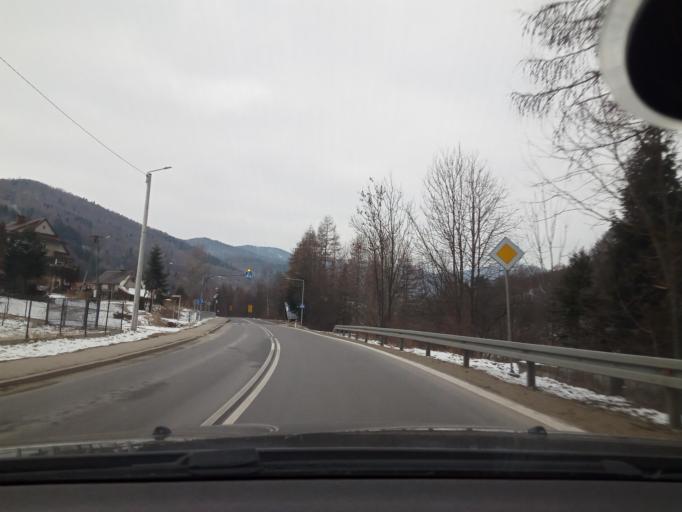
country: PL
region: Lesser Poland Voivodeship
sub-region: Powiat nowotarski
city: Kroscienko nad Dunajcem
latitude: 49.4758
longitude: 20.4317
